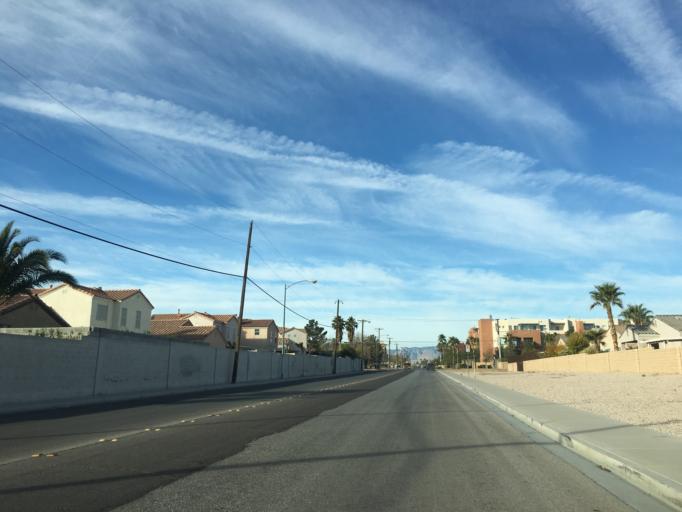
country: US
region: Nevada
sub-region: Clark County
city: Enterprise
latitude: 36.0209
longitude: -115.1662
